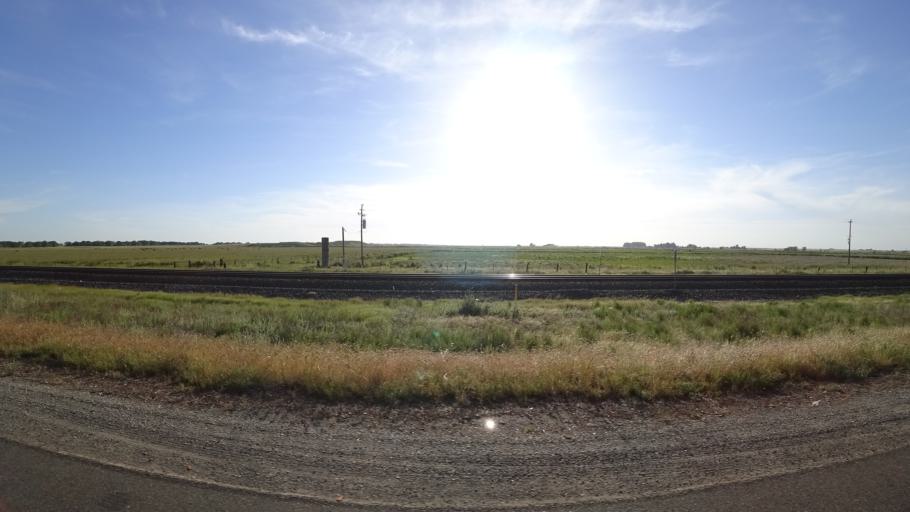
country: US
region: California
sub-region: Placer County
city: Sheridan
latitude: 38.9451
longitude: -121.3554
